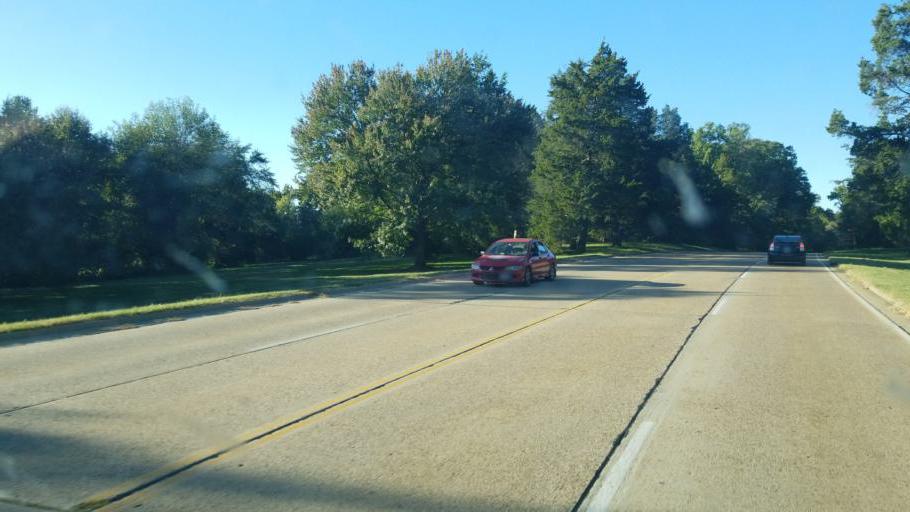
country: US
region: Virginia
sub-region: Fairfax County
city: Fort Hunt
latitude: 38.7348
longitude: -77.0487
